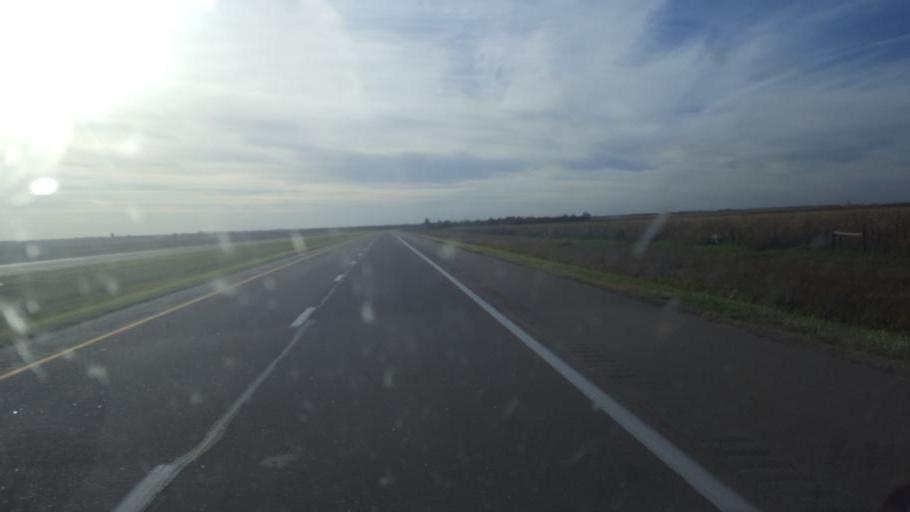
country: US
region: Kansas
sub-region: Trego County
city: WaKeeney
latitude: 39.0240
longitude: -100.1503
